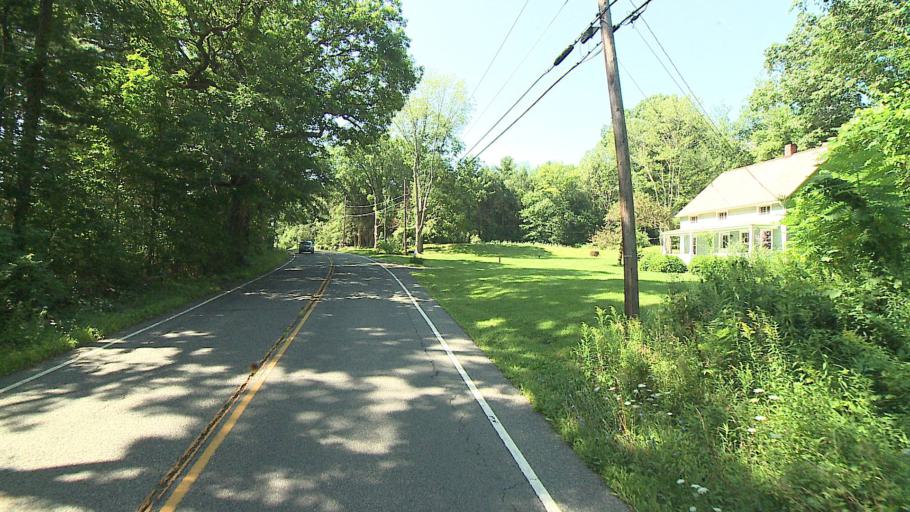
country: US
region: Connecticut
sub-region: Litchfield County
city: Canaan
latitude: 42.0357
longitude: -73.4278
